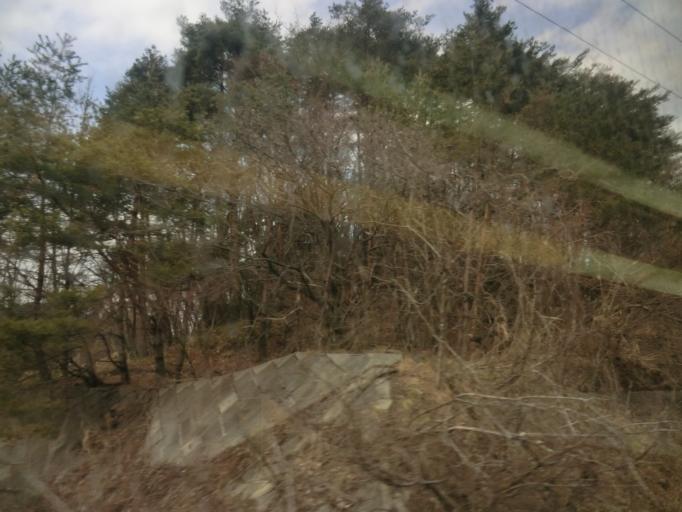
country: JP
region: Nagano
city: Hotaka
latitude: 36.3965
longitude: 138.0075
